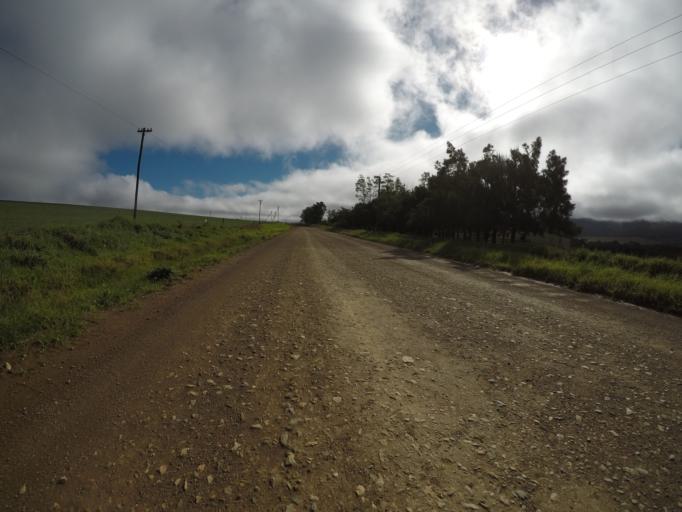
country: ZA
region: Western Cape
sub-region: Cape Winelands District Municipality
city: Ashton
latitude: -34.1319
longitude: 19.8548
